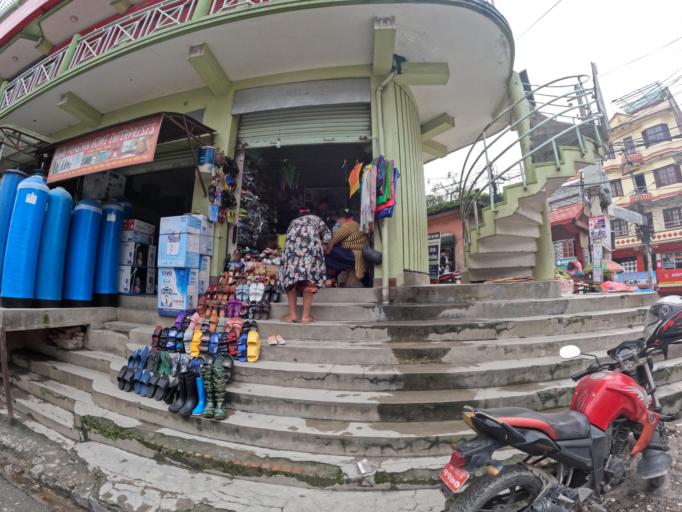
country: NP
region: Central Region
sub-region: Bagmati Zone
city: Kathmandu
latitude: 27.7477
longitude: 85.3176
